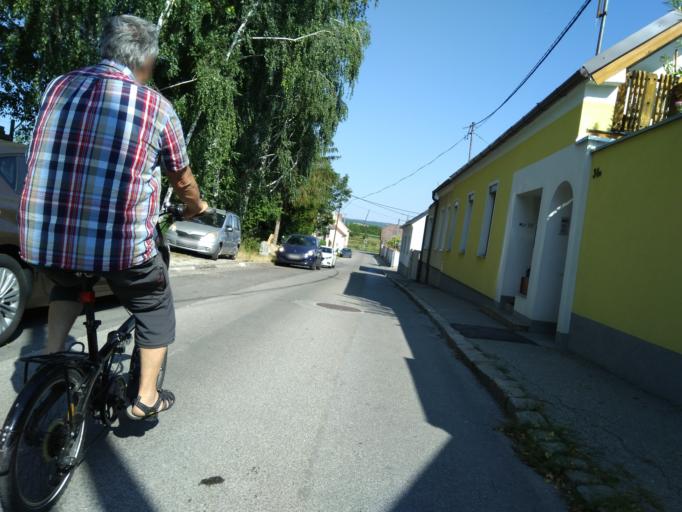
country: AT
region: Lower Austria
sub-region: Politischer Bezirk Mistelbach
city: Wolkersdorf im Weinviertel
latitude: 48.3832
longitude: 16.5091
